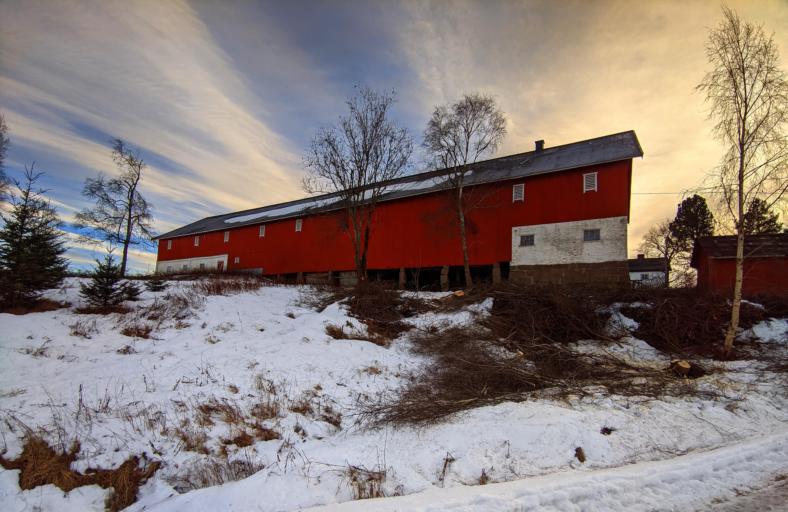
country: NO
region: Akershus
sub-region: Nannestad
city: Teigebyen
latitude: 60.1664
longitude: 11.0005
